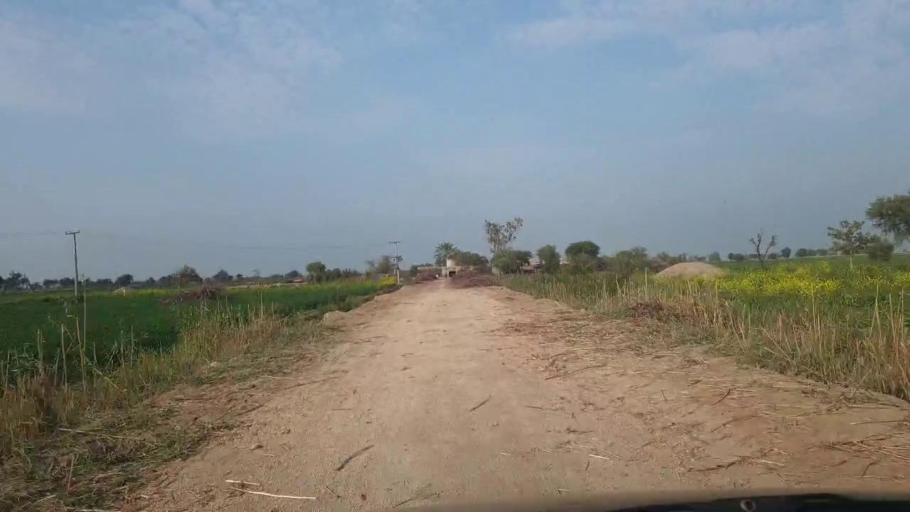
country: PK
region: Sindh
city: Shahdadpur
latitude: 25.8766
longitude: 68.7033
